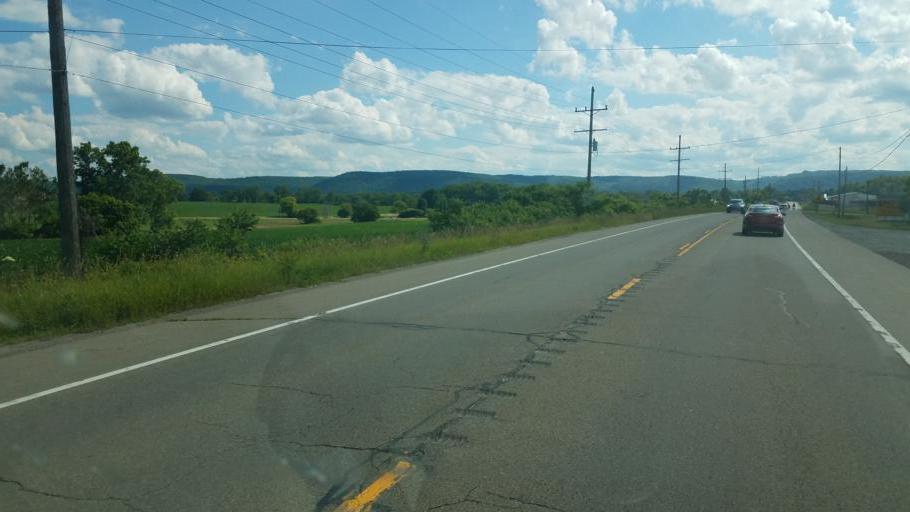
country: US
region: New York
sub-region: Steuben County
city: Bath
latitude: 42.3566
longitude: -77.2983
